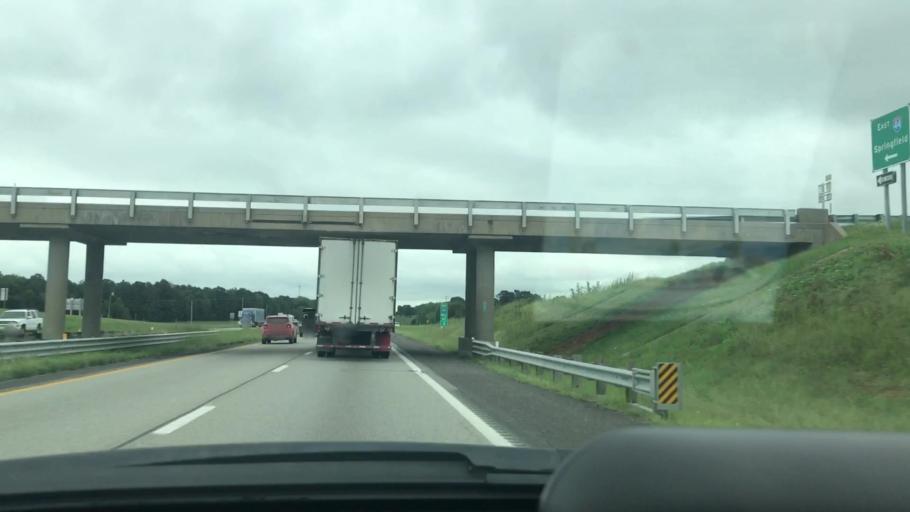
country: US
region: Missouri
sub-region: Greene County
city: Republic
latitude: 37.1858
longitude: -93.5697
